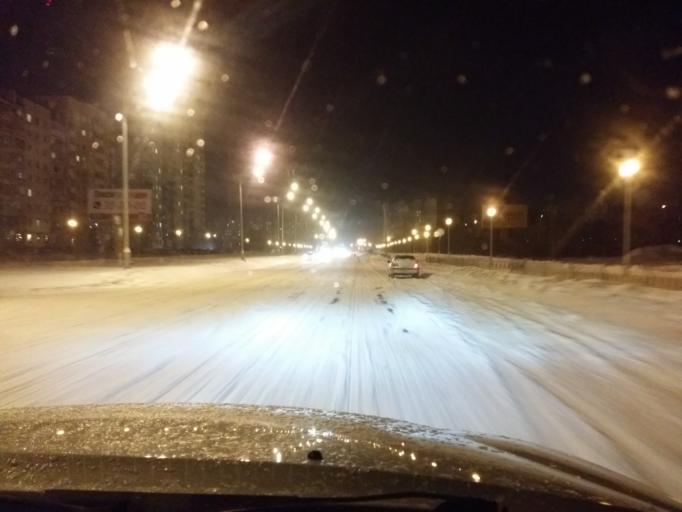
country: RU
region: Khanty-Mansiyskiy Avtonomnyy Okrug
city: Nizhnevartovsk
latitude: 60.9525
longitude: 76.5682
